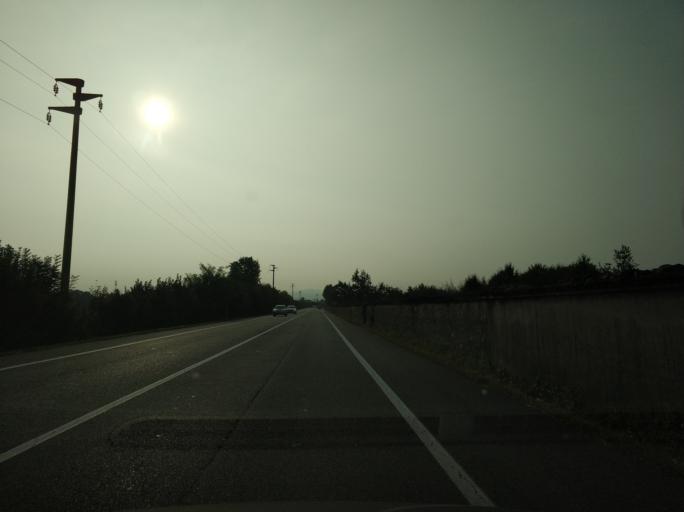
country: IT
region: Piedmont
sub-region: Provincia di Torino
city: Druento
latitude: 45.1609
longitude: 7.6040
